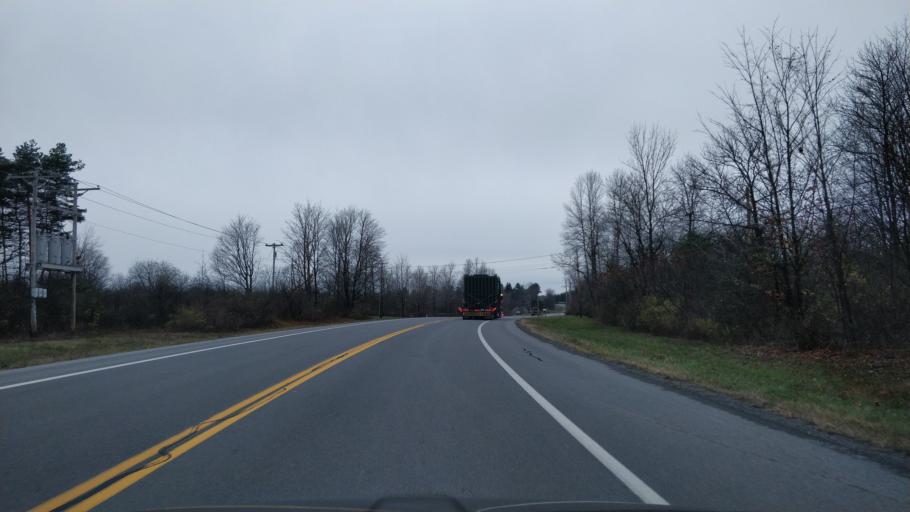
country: CA
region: Ontario
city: Brockville
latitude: 44.6139
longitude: -75.5993
